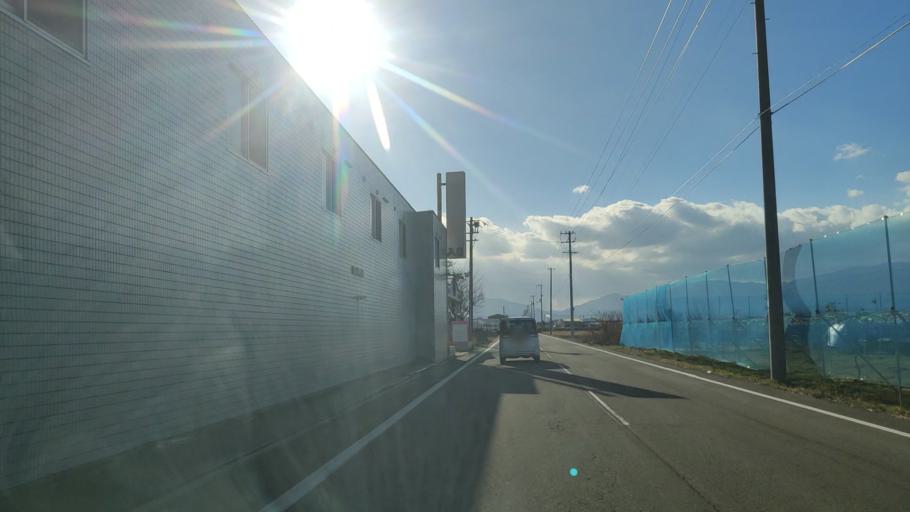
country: JP
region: Ehime
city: Saijo
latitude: 33.9146
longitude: 133.1177
